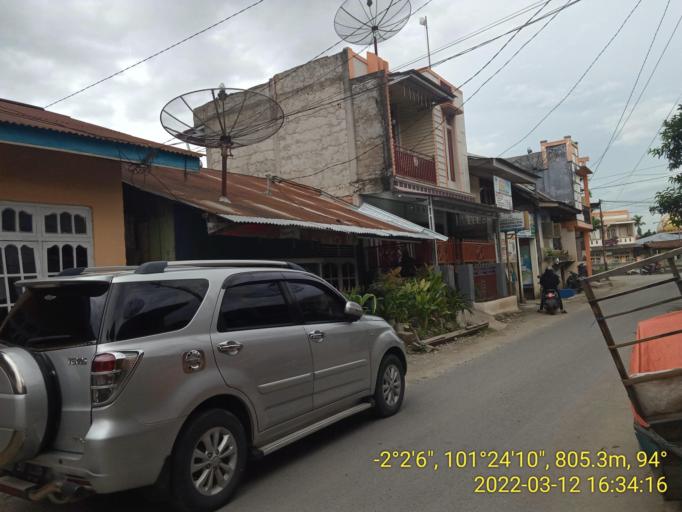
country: ID
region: Jambi
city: Sungai Penuh
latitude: -2.0352
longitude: 101.4029
